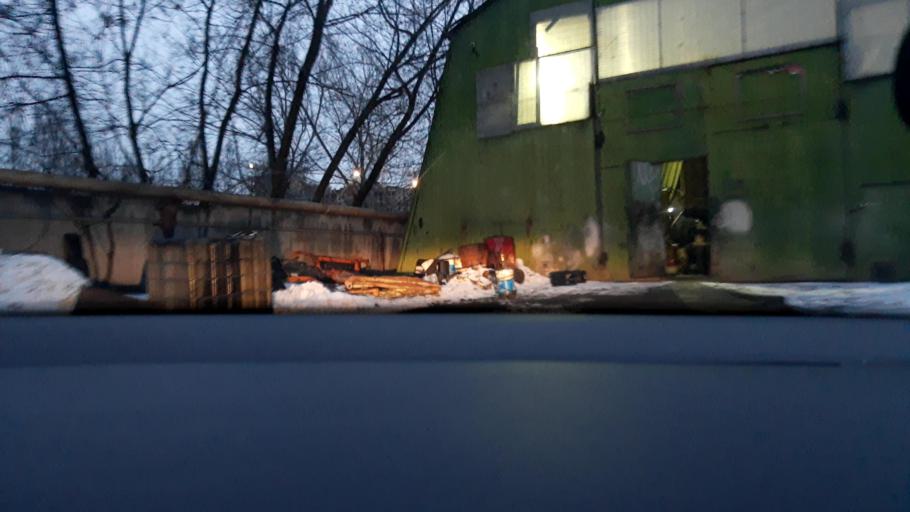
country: RU
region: Moscow
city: Tsaritsyno
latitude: 55.6093
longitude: 37.6490
